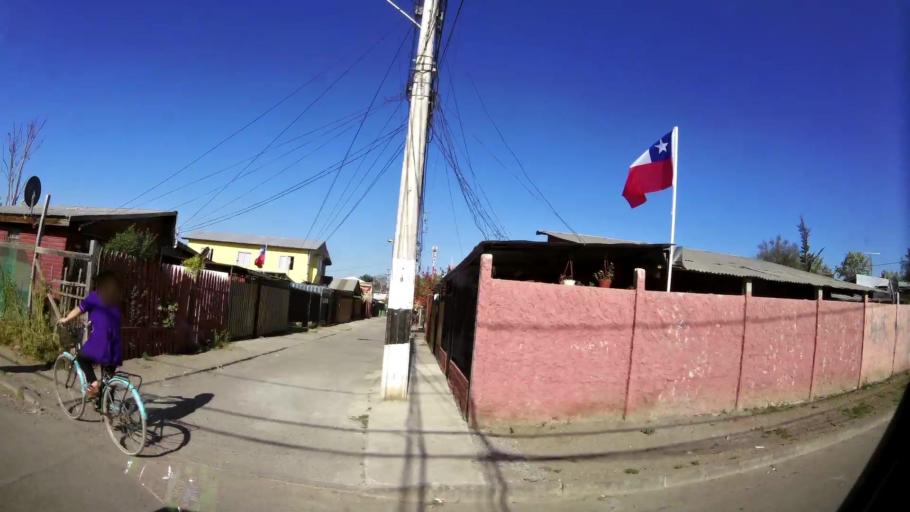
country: CL
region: Santiago Metropolitan
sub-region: Provincia de Talagante
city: Penaflor
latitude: -33.6094
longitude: -70.8720
